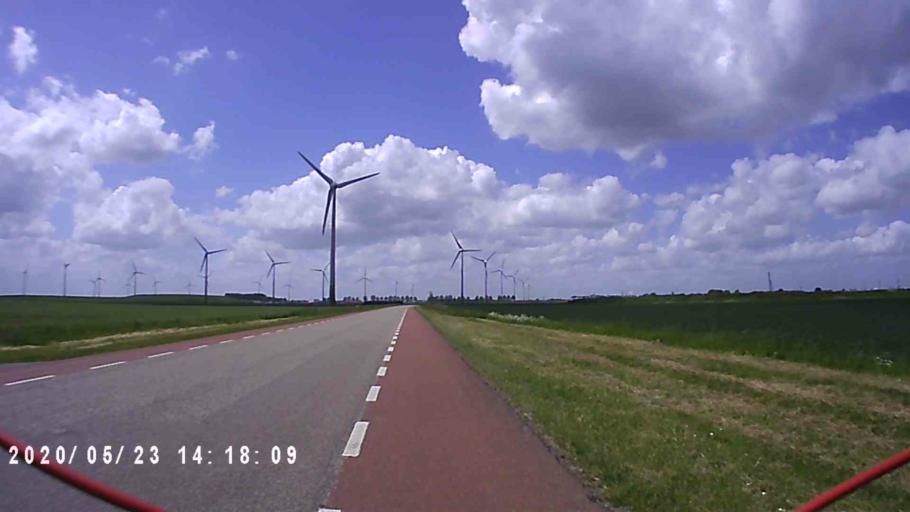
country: NL
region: Groningen
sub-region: Gemeente Delfzijl
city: Delfzijl
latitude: 53.2868
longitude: 6.9953
